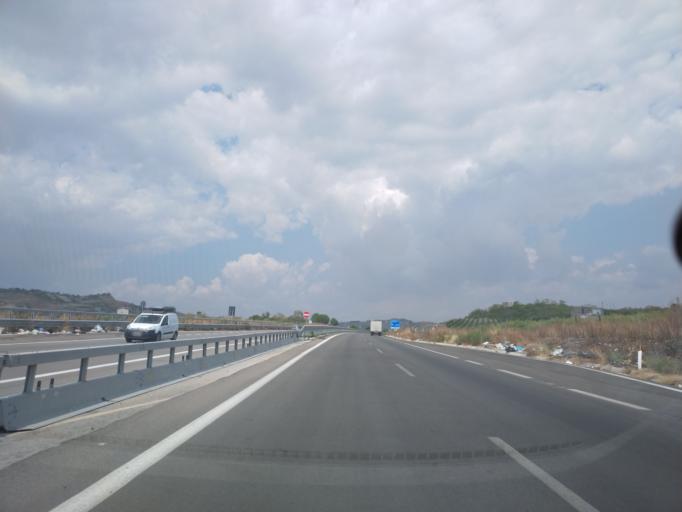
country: IT
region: Sicily
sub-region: Agrigento
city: Grotte
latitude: 37.3661
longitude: 13.7046
